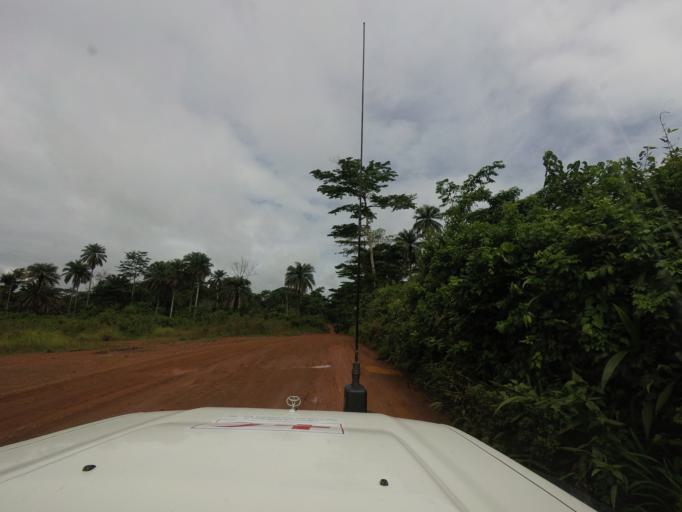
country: GN
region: Nzerekore
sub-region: Nzerekore Prefecture
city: Nzerekore
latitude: 7.7236
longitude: -8.8787
